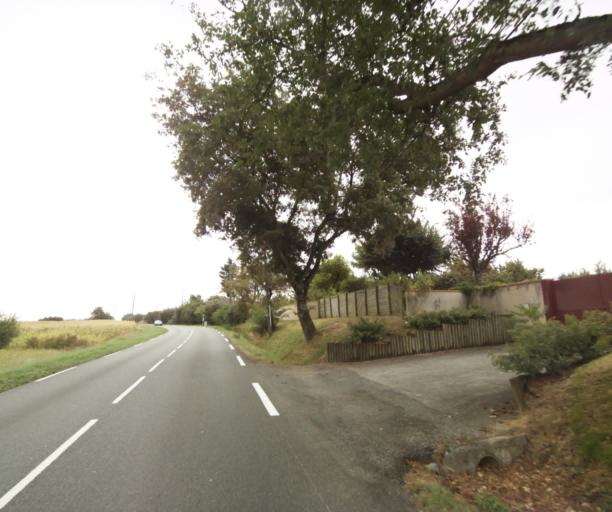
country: FR
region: Midi-Pyrenees
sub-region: Departement de la Haute-Garonne
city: Flourens
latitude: 43.5989
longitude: 1.5317
